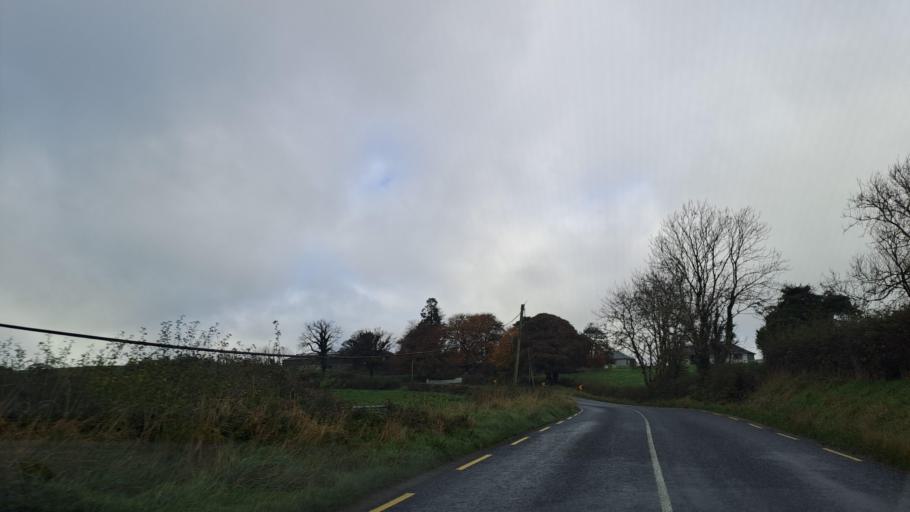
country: IE
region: Ulster
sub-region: An Cabhan
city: Bailieborough
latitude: 53.8968
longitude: -7.0103
